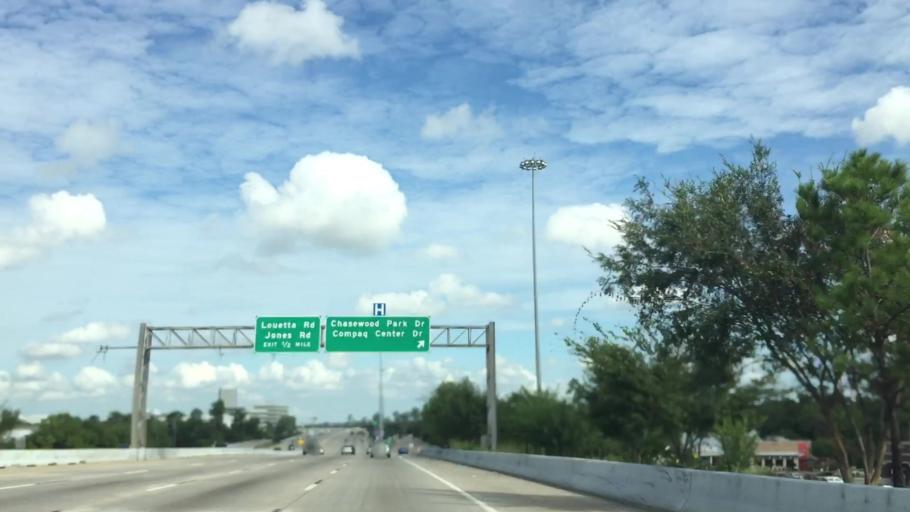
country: US
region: Texas
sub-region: Harris County
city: Oak Cliff Place
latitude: 29.9817
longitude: -95.5677
